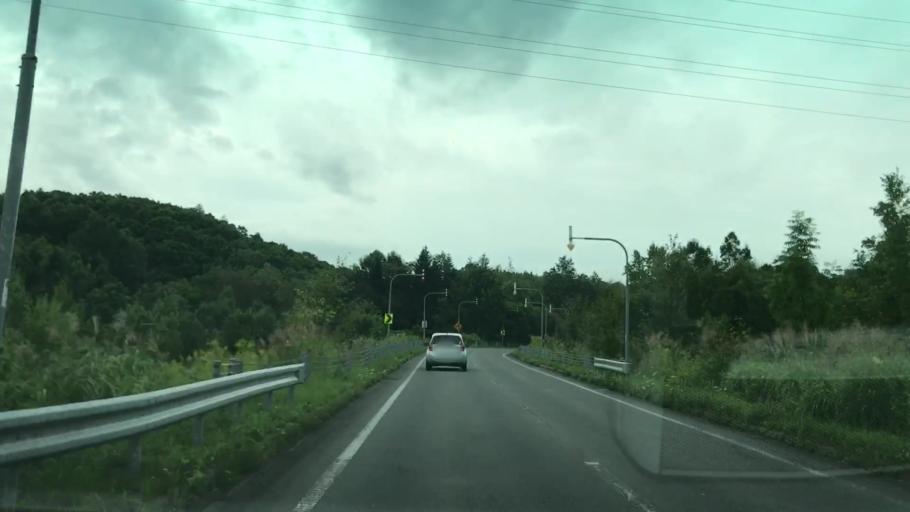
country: JP
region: Hokkaido
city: Yoichi
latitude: 43.1409
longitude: 140.8206
